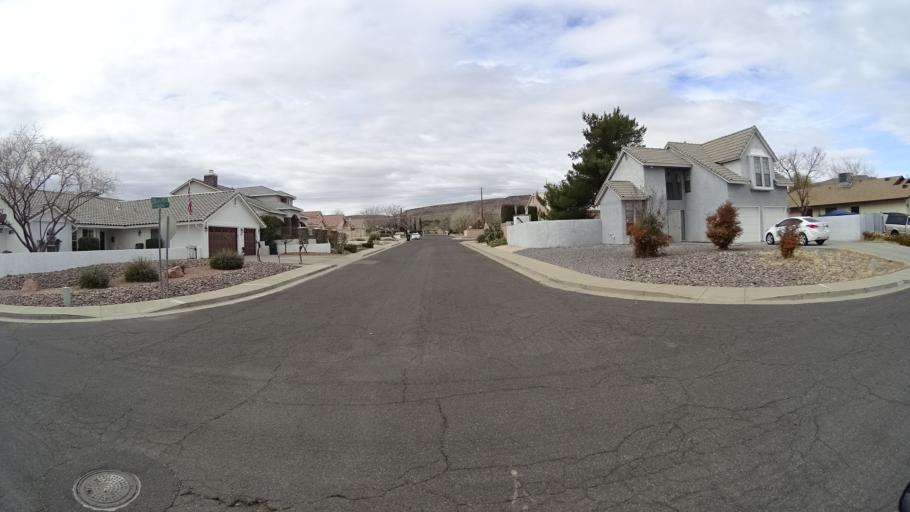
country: US
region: Arizona
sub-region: Mohave County
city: New Kingman-Butler
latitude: 35.2345
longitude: -114.0389
